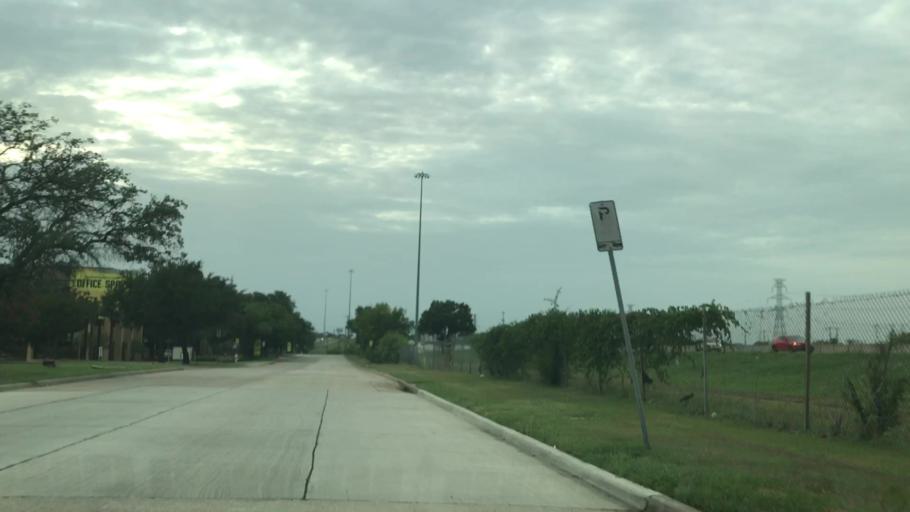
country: US
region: Texas
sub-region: Dallas County
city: Garland
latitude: 32.8814
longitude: -96.6938
